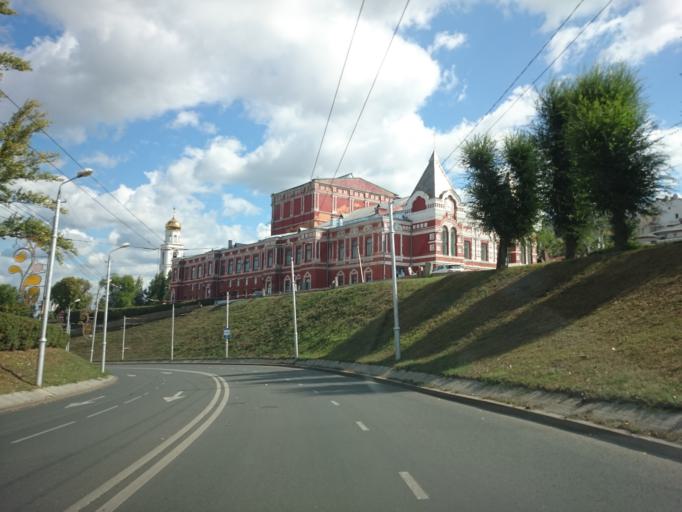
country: RU
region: Samara
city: Samara
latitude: 53.1971
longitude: 50.0959
